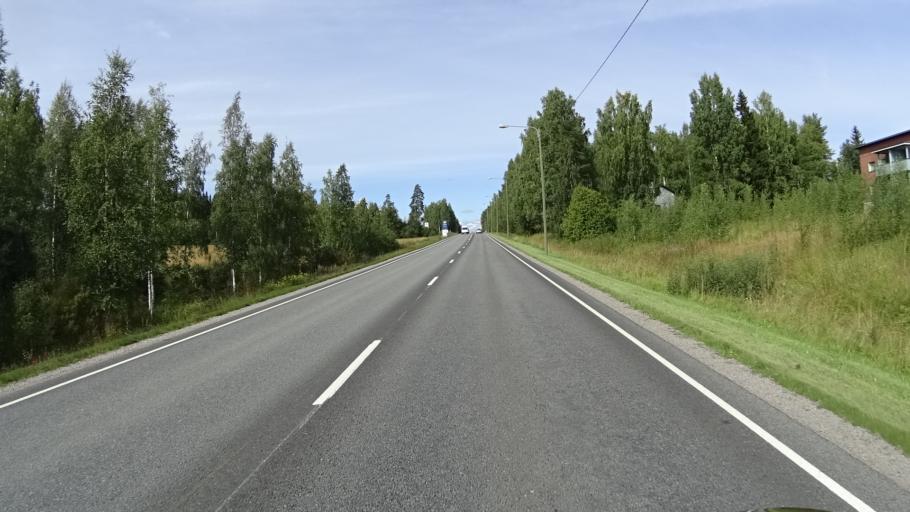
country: FI
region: Pirkanmaa
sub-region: Tampere
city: Haemeenkyroe
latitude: 61.6475
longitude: 23.1845
